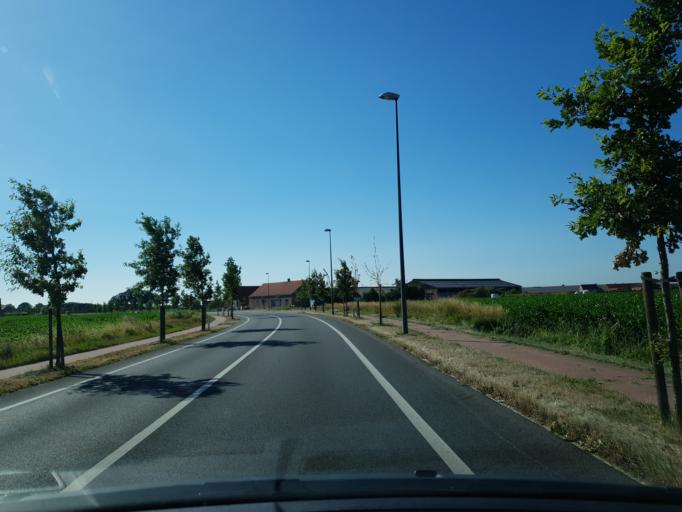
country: BE
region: Flanders
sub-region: Provincie Antwerpen
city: Brecht
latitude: 51.4030
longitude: 4.6762
